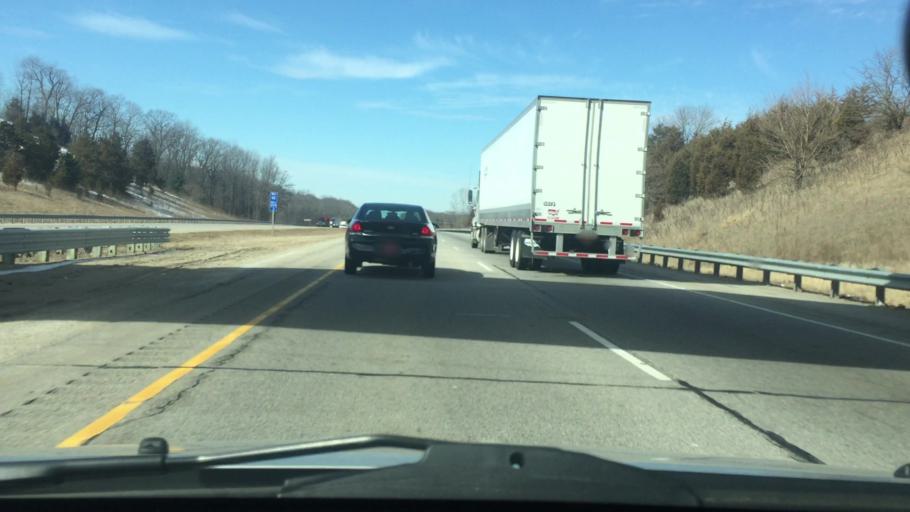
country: US
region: Wisconsin
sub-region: Jefferson County
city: Waterloo
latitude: 43.1109
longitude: -89.0083
